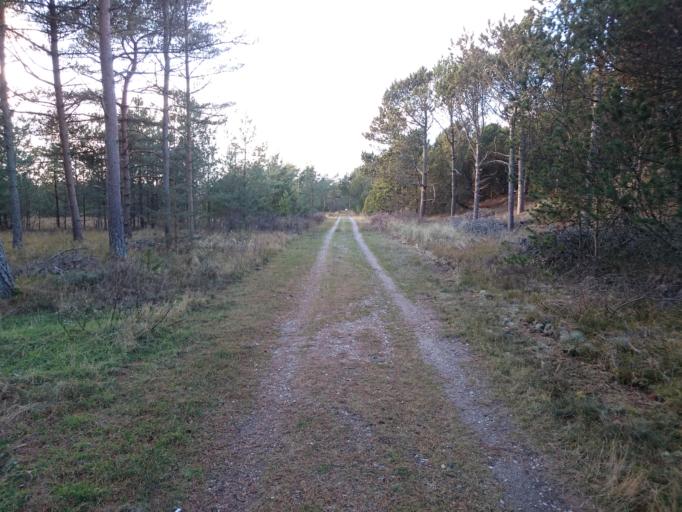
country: DK
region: North Denmark
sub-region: Frederikshavn Kommune
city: Skagen
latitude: 57.7075
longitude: 10.5284
